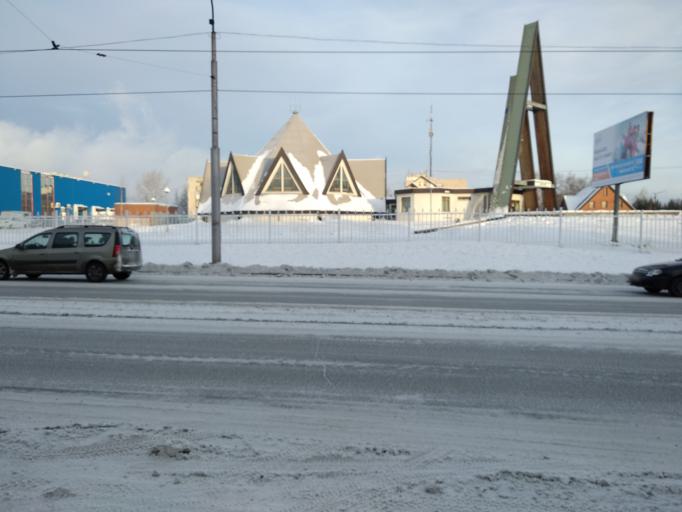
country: RU
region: Sverdlovsk
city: Krasnotur'insk
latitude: 59.7664
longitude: 60.2067
